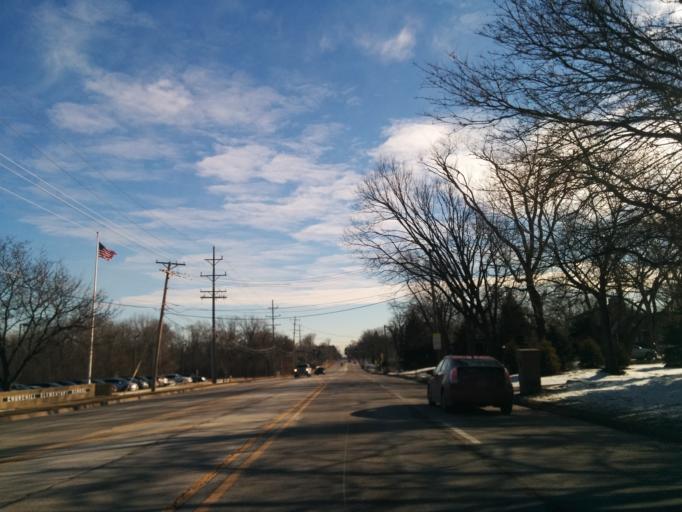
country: US
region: Illinois
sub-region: DuPage County
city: Glen Ellyn
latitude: 41.8889
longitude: -88.0811
